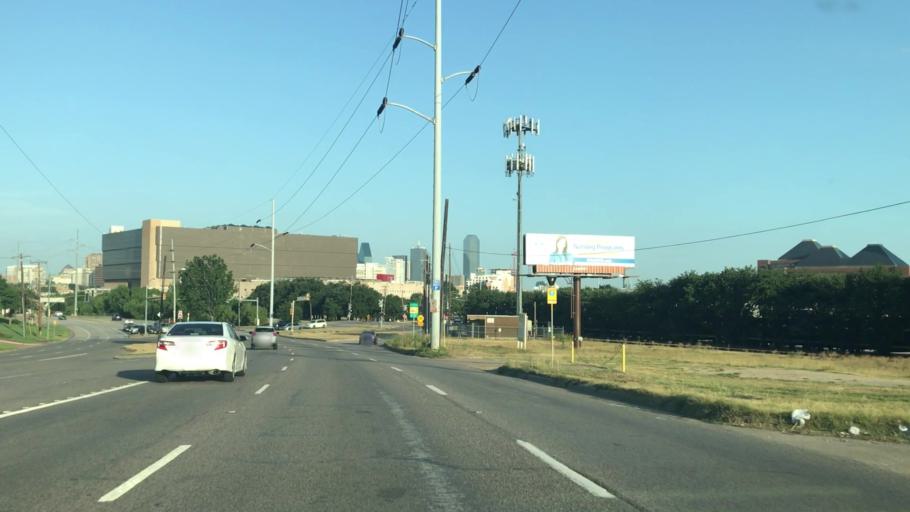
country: US
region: Texas
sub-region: Dallas County
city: Dallas
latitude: 32.8068
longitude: -96.8312
